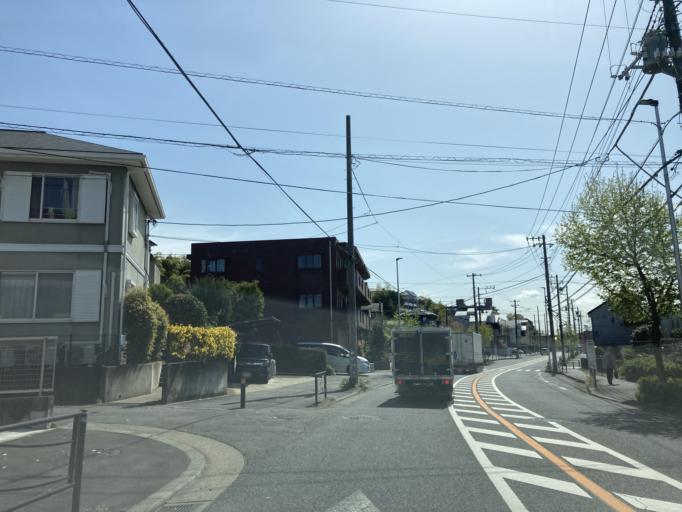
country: JP
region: Tokyo
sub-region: Machida-shi
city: Machida
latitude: 35.6035
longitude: 139.4812
